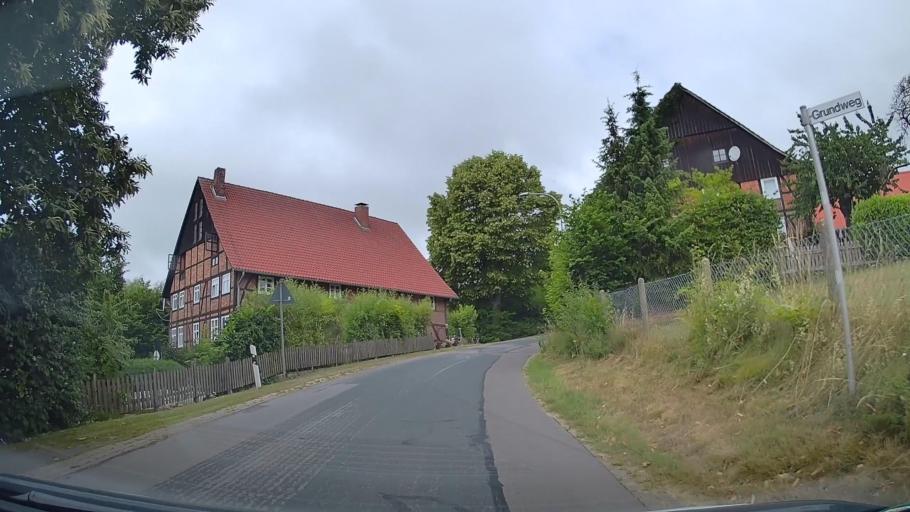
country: DE
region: Lower Saxony
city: Aerzen
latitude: 52.0513
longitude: 9.1769
